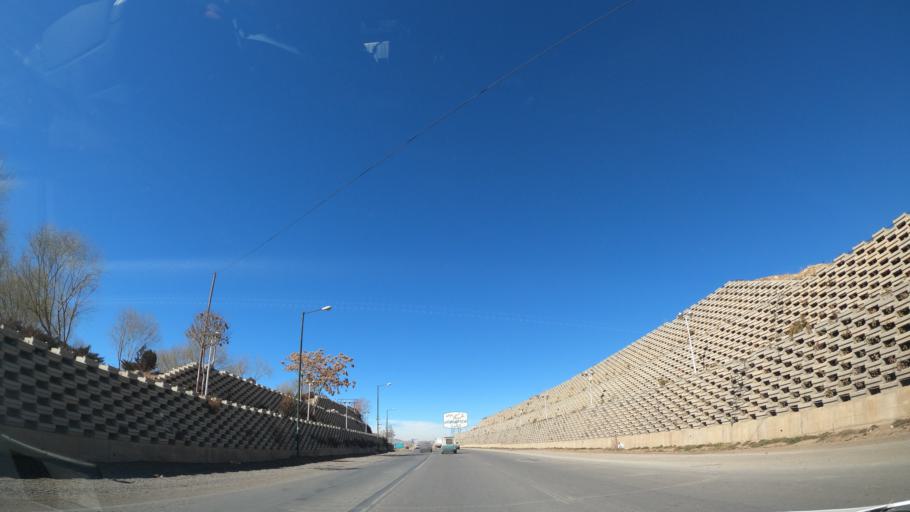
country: IR
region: Chahar Mahall va Bakhtiari
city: Shahrekord
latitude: 32.3071
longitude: 50.9077
